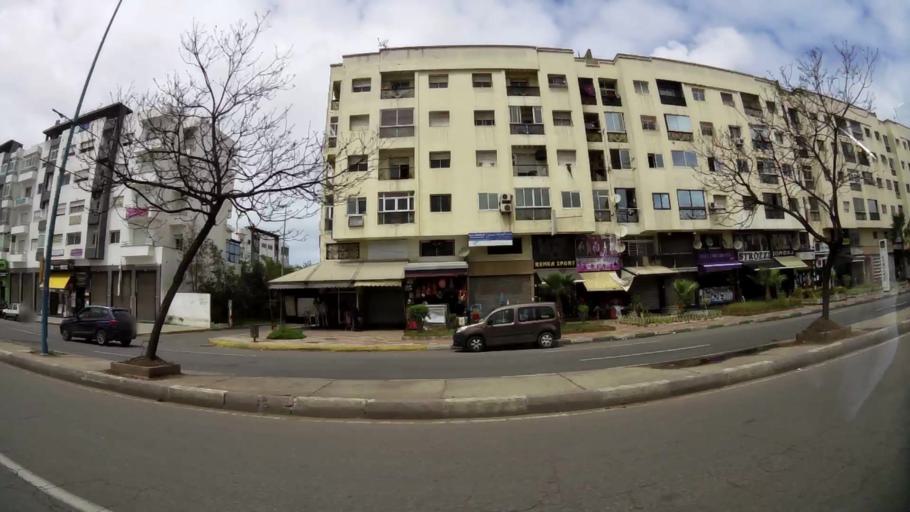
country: MA
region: Grand Casablanca
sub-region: Casablanca
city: Casablanca
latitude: 33.5386
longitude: -7.6016
